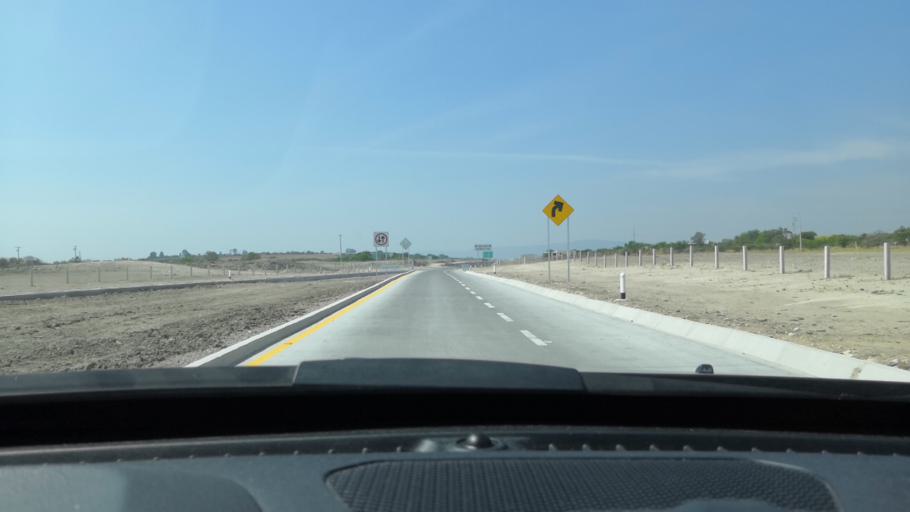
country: MX
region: Guanajuato
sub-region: Leon
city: Malagana (San Antonio del Monte)
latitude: 21.0922
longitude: -101.7913
